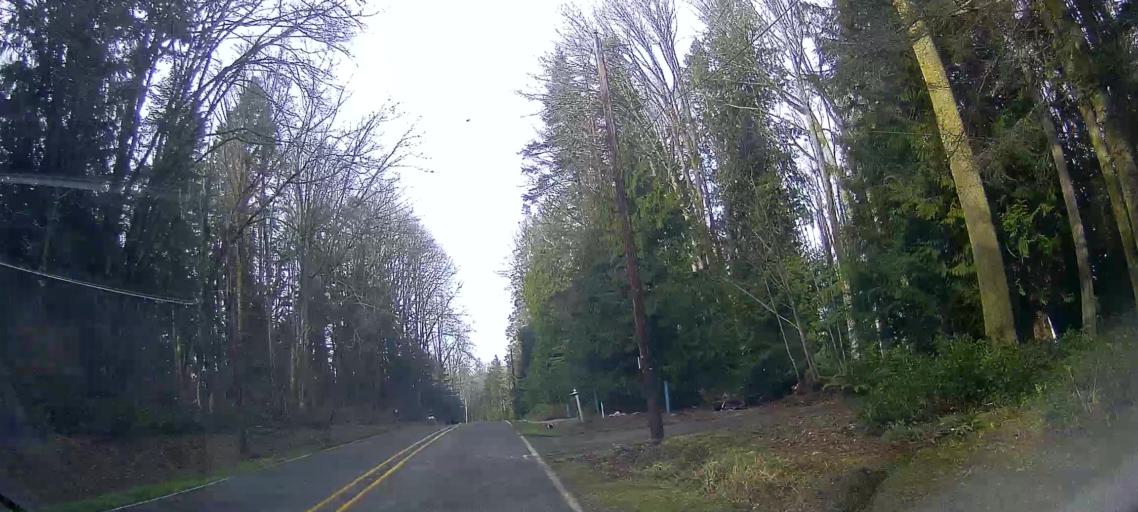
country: US
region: Washington
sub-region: Island County
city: Langley
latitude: 48.0823
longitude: -122.3787
